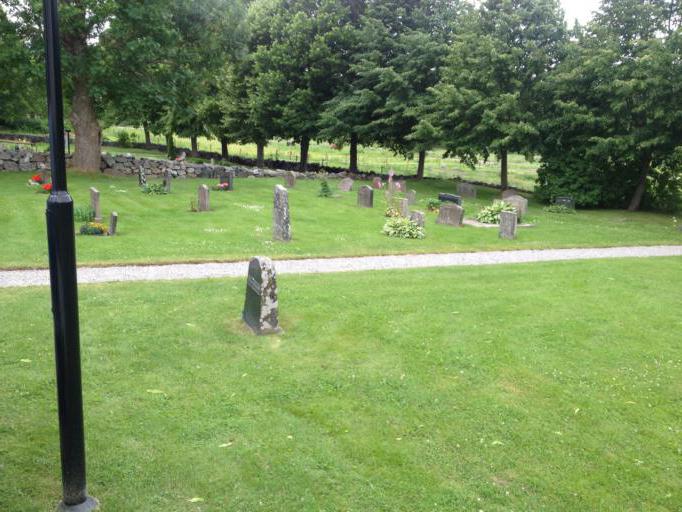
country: SE
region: Stockholm
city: Stenhamra
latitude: 59.4010
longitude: 17.5607
